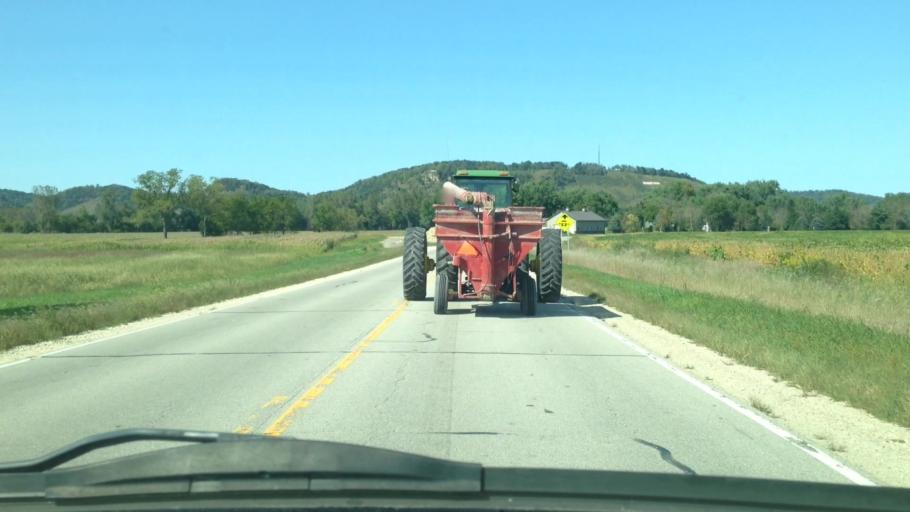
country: US
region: Minnesota
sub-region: Fillmore County
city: Rushford
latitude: 43.7908
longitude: -91.7652
